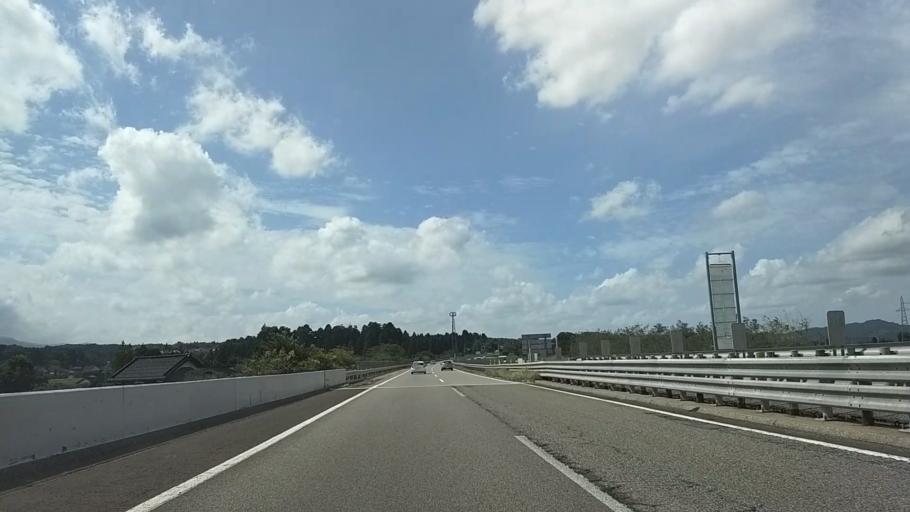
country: JP
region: Toyama
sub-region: Oyabe Shi
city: Oyabe
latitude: 36.6293
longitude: 136.8836
